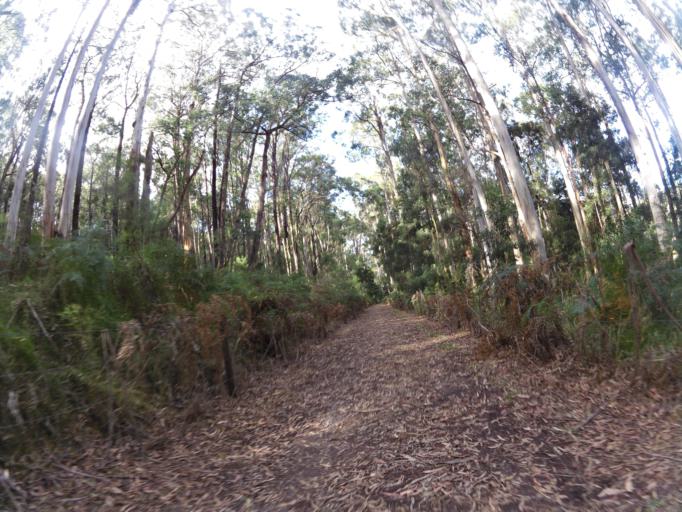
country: AU
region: Victoria
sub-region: Colac-Otway
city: Colac
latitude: -38.4942
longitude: 143.7355
